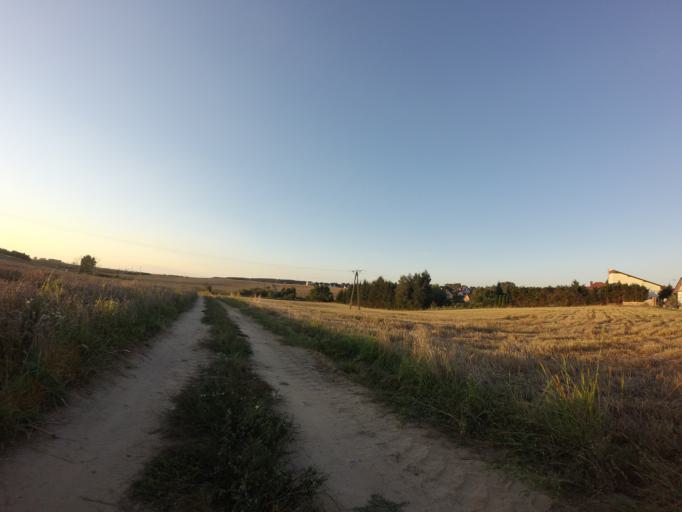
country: PL
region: West Pomeranian Voivodeship
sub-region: Powiat choszczenski
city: Choszczno
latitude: 53.1805
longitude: 15.4118
